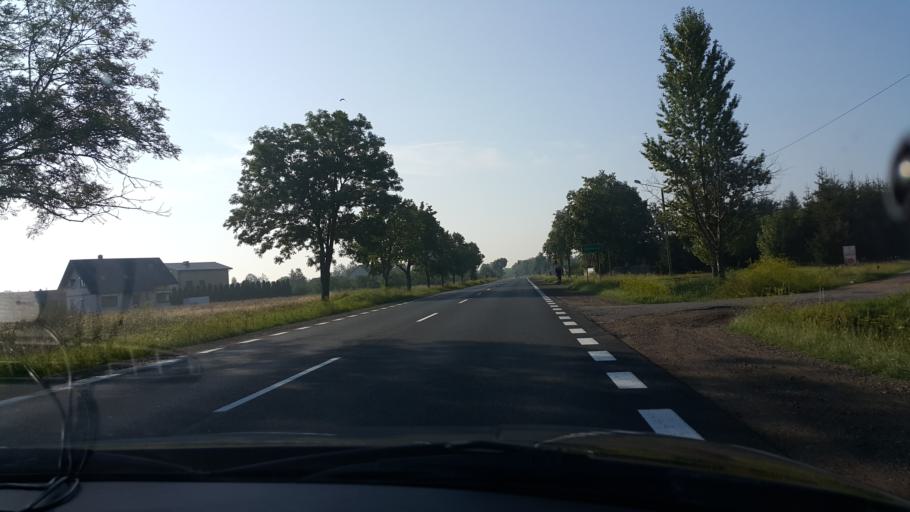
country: PL
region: Masovian Voivodeship
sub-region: Powiat radomski
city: Jedlnia-Letnisko
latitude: 51.4057
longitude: 21.2471
